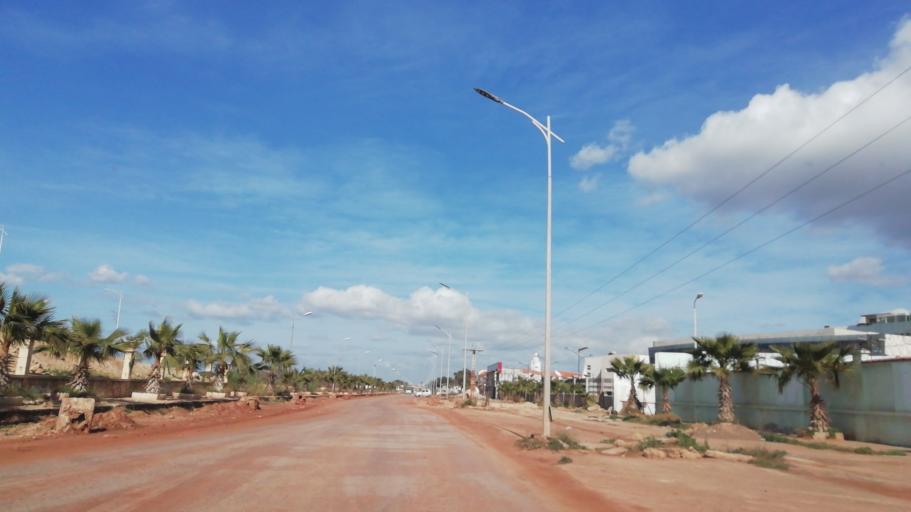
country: DZ
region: Oran
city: Es Senia
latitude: 35.6258
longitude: -0.5842
